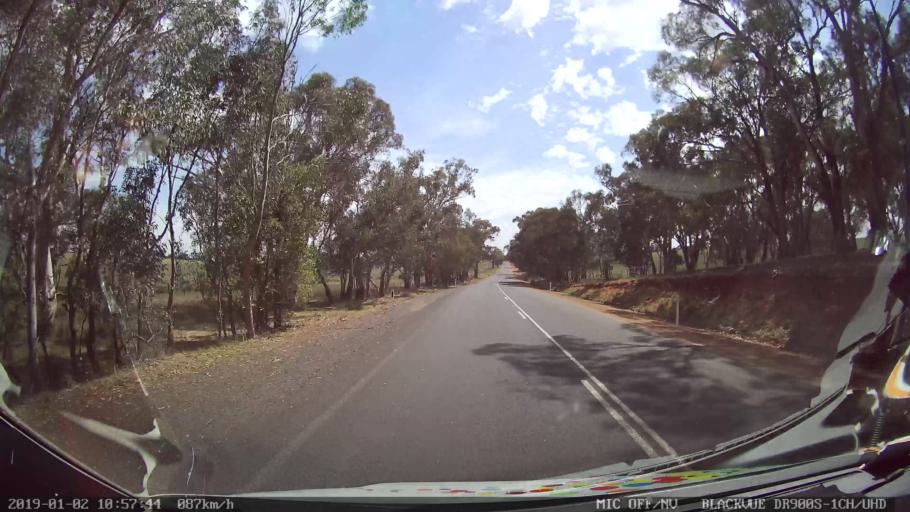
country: AU
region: New South Wales
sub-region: Cootamundra
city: Cootamundra
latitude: -34.6319
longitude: 148.2847
